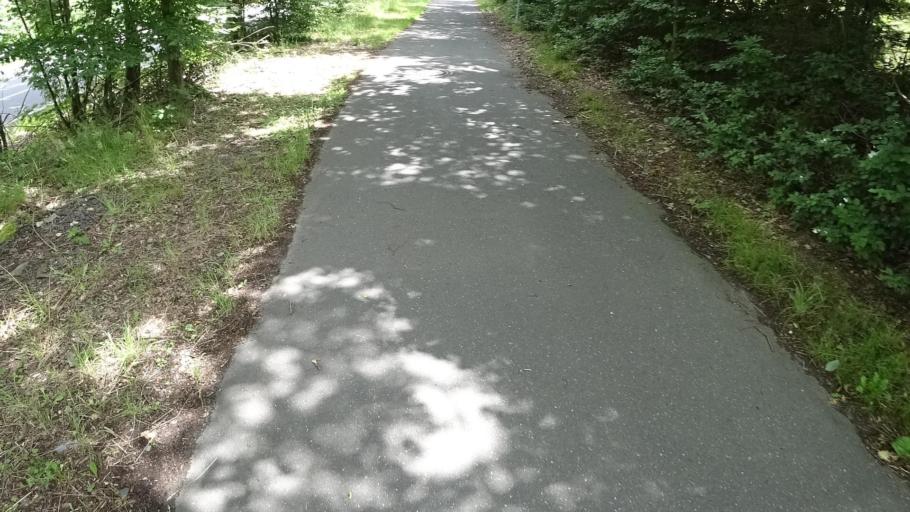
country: DE
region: Rheinland-Pfalz
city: Vettelschoss
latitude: 50.6230
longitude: 7.3386
